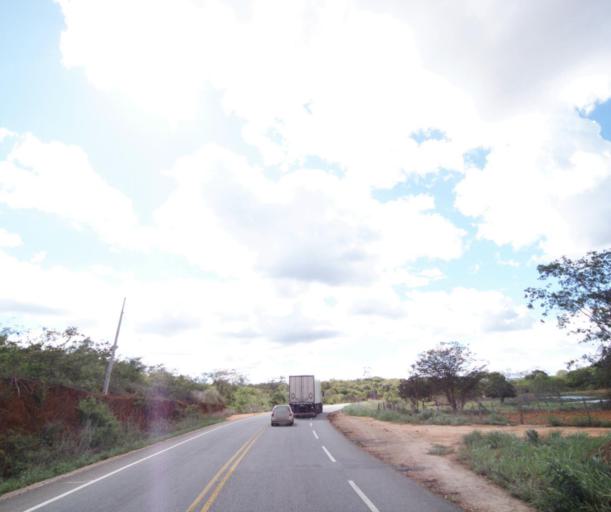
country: BR
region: Bahia
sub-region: Caetite
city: Caetite
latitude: -14.1369
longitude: -42.3840
